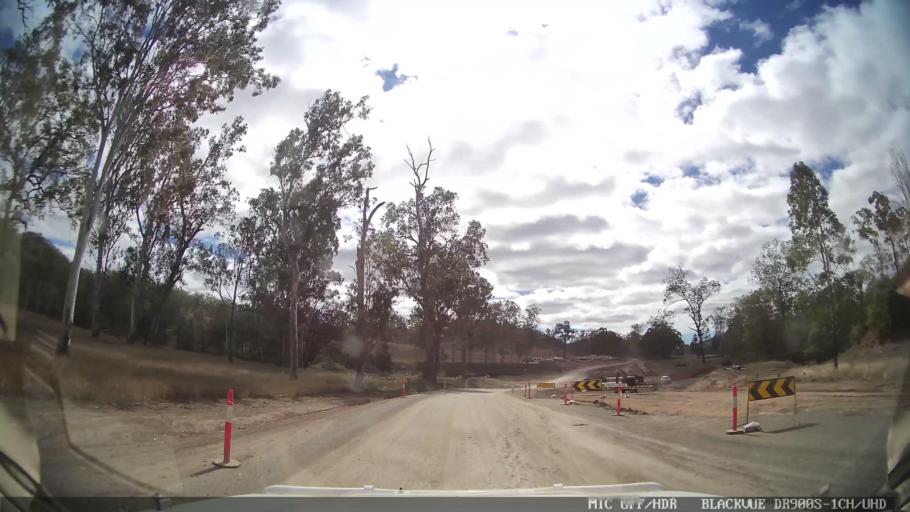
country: AU
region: Queensland
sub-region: Gladstone
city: Toolooa
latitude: -24.6153
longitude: 151.2990
